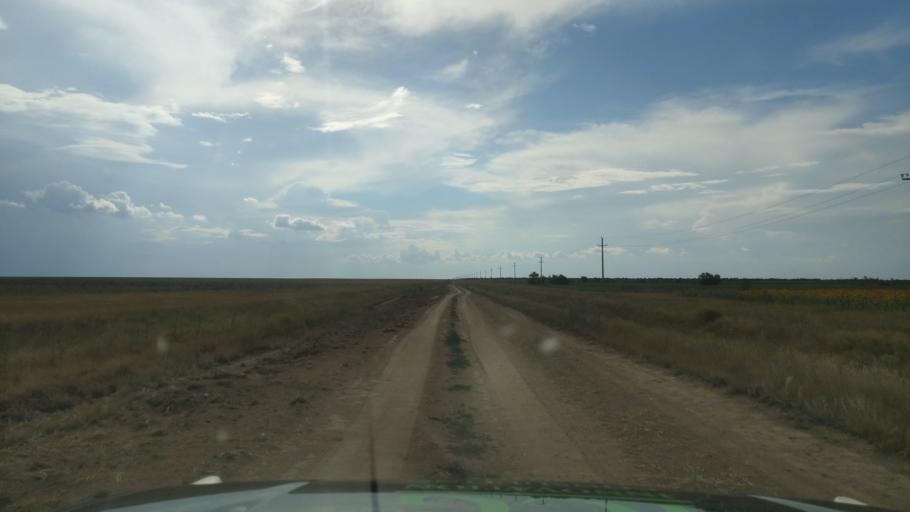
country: KZ
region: Pavlodar
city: Pavlodar
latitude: 52.5122
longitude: 77.5403
